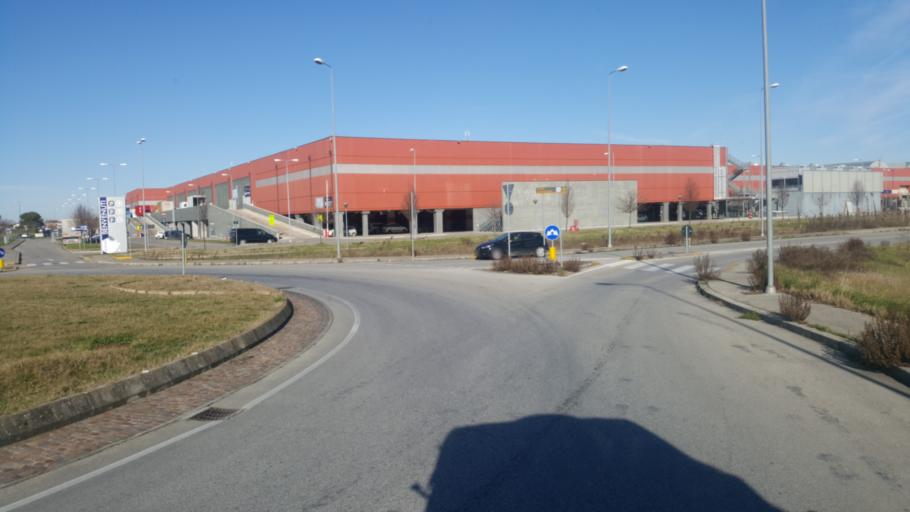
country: IT
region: Emilia-Romagna
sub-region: Forli-Cesena
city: Forli
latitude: 44.2421
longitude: 12.0838
